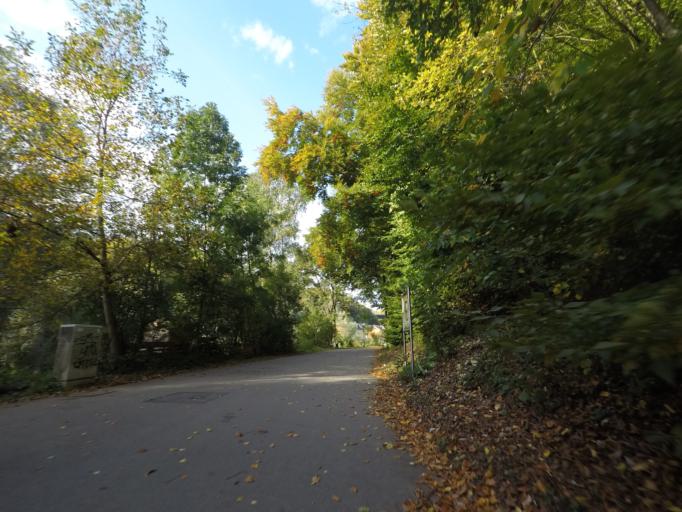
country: LU
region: Luxembourg
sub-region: Canton de Luxembourg
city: Hesperange
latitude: 49.5748
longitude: 6.1545
